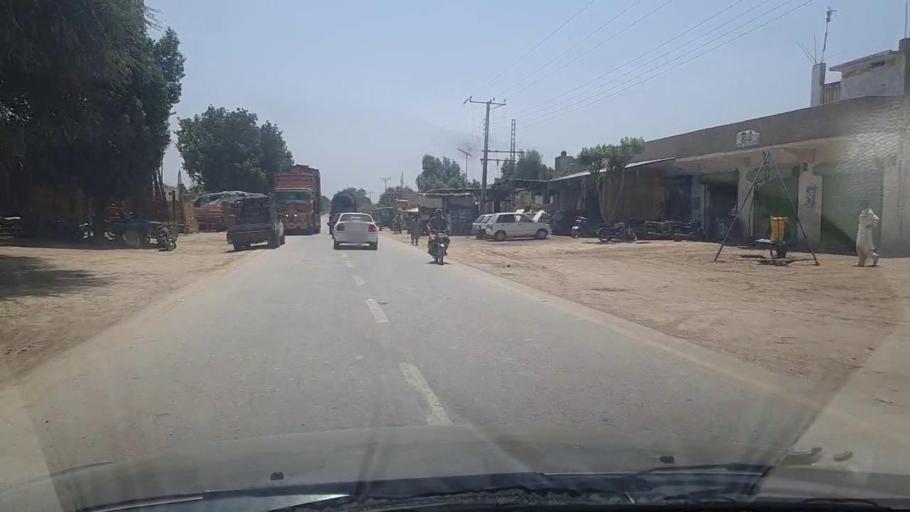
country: PK
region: Sindh
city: Tando Jam
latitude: 25.3074
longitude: 68.5776
